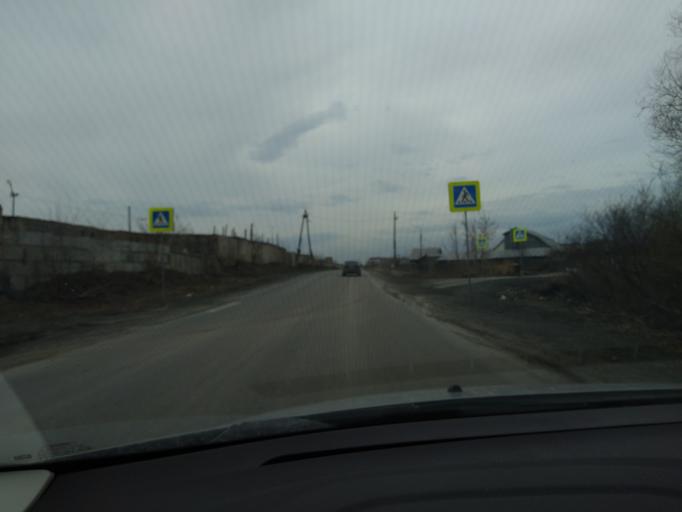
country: RU
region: Chelyabinsk
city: Potanino
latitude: 55.2883
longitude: 61.5307
